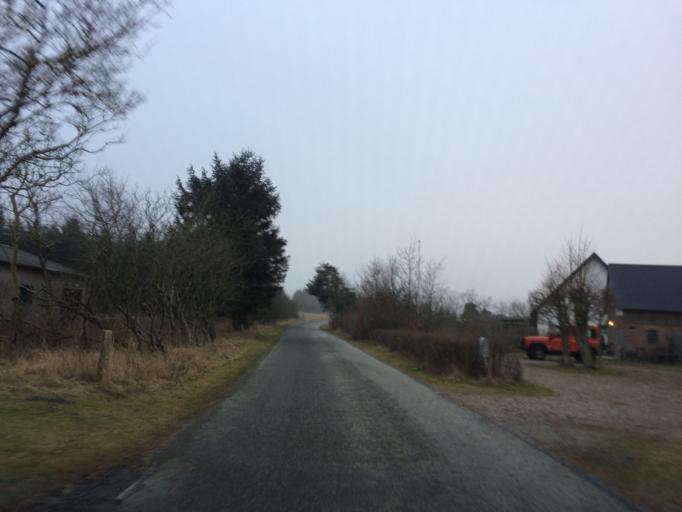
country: DK
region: South Denmark
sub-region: Varde Kommune
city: Oksbol
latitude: 55.5773
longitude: 8.3224
